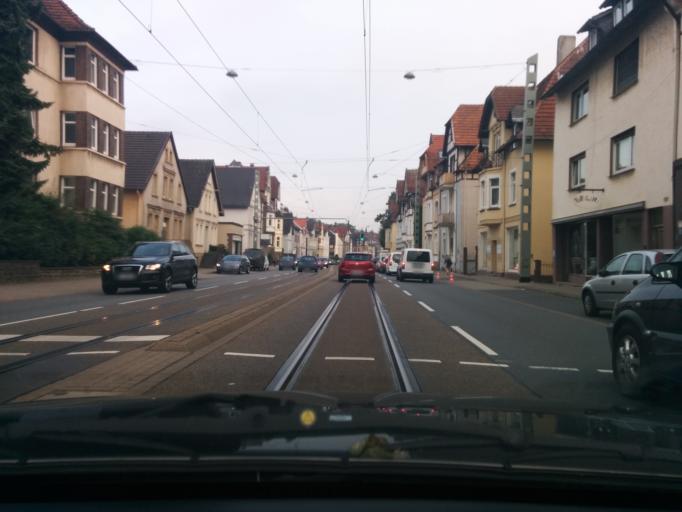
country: DE
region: North Rhine-Westphalia
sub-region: Regierungsbezirk Detmold
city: Bielefeld
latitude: 52.0077
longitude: 8.5458
